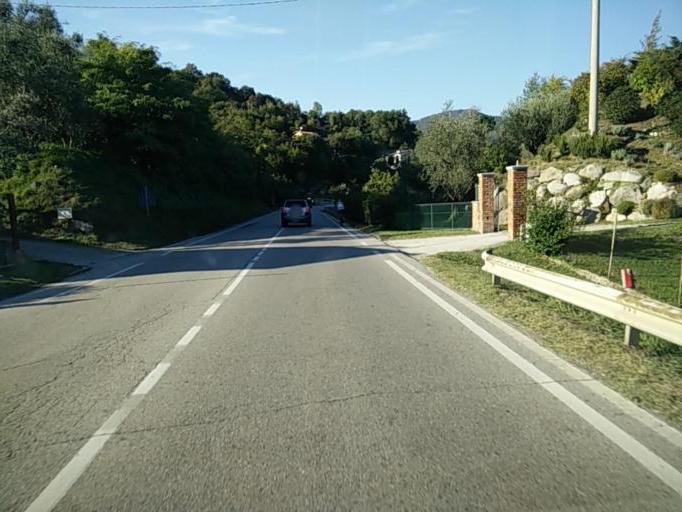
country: IT
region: Lombardy
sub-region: Provincia di Brescia
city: Roe Volciano
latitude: 45.6027
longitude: 10.5011
